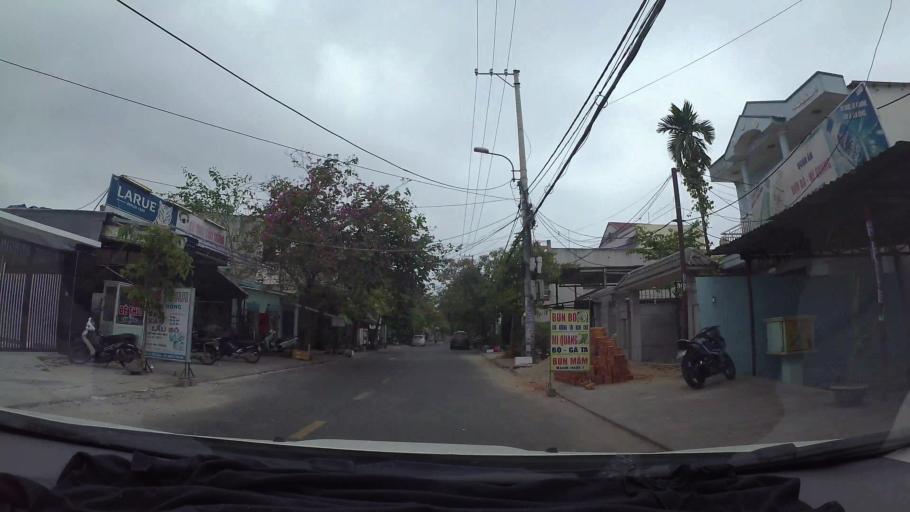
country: VN
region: Da Nang
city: Lien Chieu
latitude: 16.0573
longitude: 108.1686
